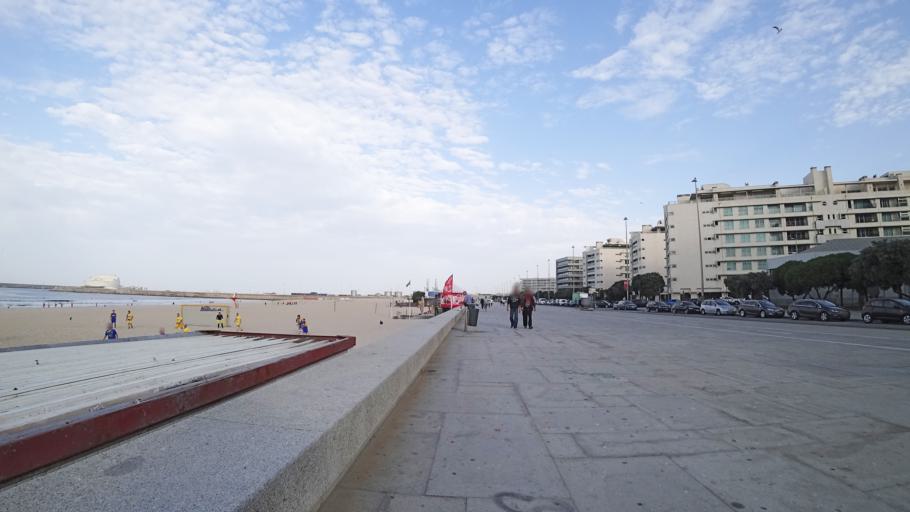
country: PT
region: Porto
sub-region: Matosinhos
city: Matosinhos
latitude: 41.1758
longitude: -8.6909
